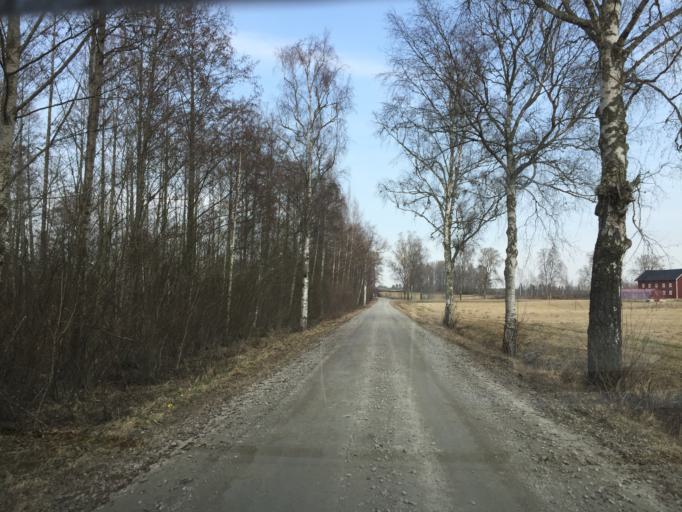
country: SE
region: Soedermanland
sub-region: Vingakers Kommun
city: Vingaker
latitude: 59.0423
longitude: 15.7864
